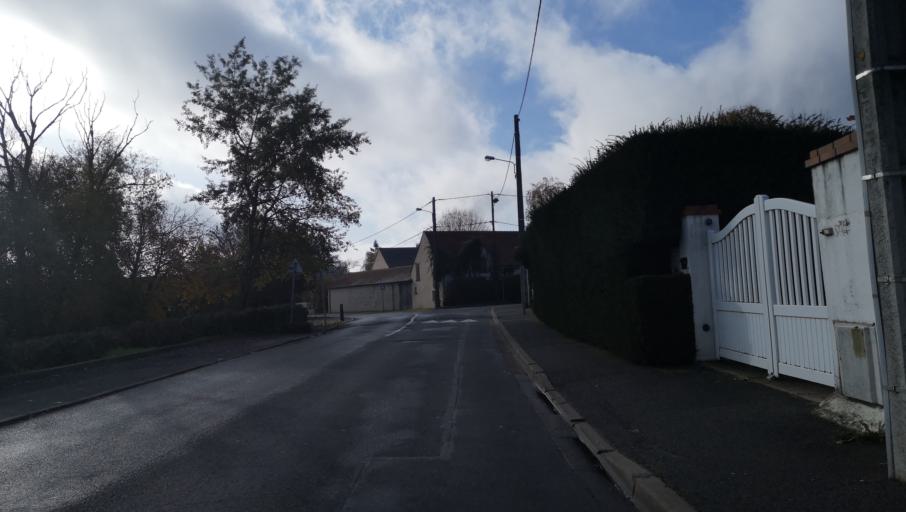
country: FR
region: Centre
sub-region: Departement du Loiret
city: Semoy
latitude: 47.9159
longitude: 1.9389
